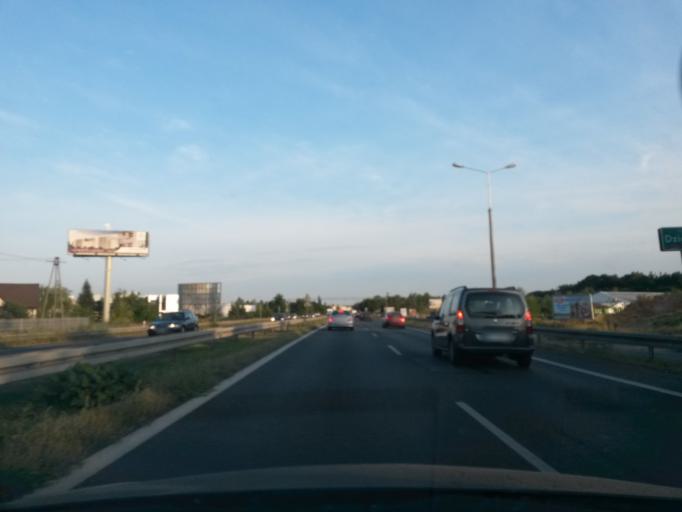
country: PL
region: Masovian Voivodeship
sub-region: Powiat warszawski zachodni
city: Kielpin
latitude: 52.3465
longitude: 20.8618
